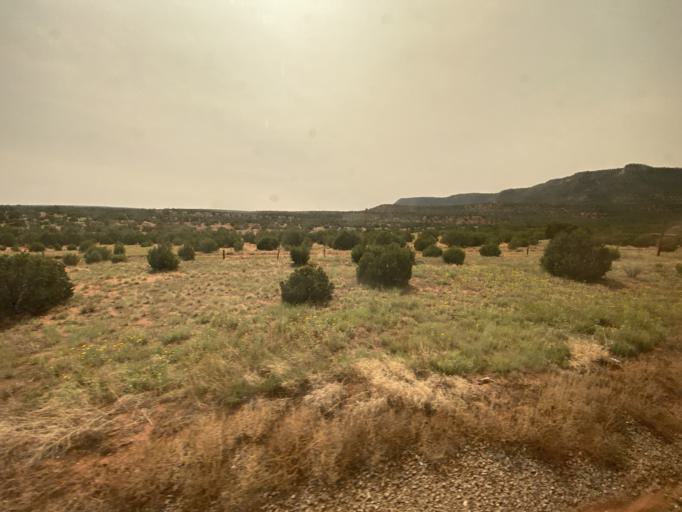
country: US
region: New Mexico
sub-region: San Miguel County
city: Pecos
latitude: 35.3953
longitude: -105.4889
